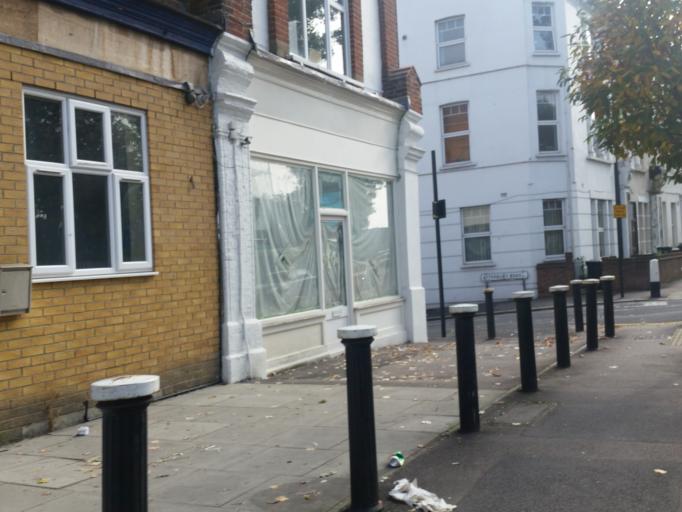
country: GB
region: England
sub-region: Greater London
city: Harringay
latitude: 51.5766
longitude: -0.1041
